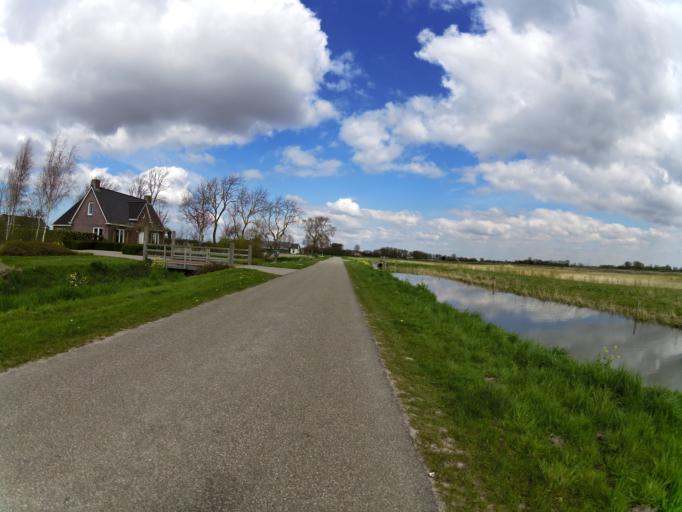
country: NL
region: South Holland
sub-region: Gemeente Hellevoetsluis
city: Nieuw-Helvoet
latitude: 51.8853
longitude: 4.0880
